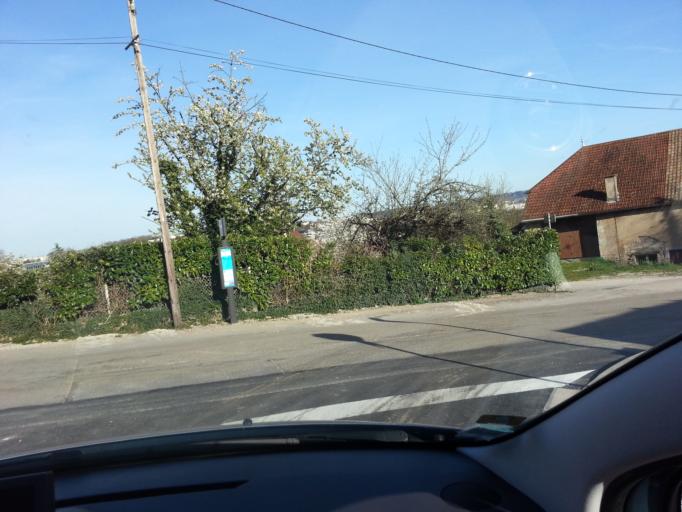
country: FR
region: Franche-Comte
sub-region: Departement du Doubs
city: Pirey
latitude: 47.2551
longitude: 5.9872
